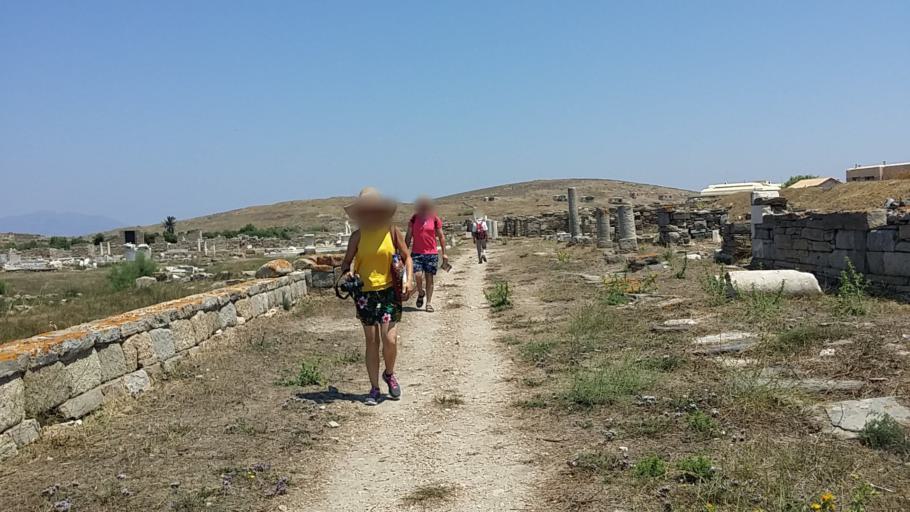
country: GR
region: South Aegean
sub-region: Nomos Kykladon
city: Mykonos
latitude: 37.4003
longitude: 25.2679
